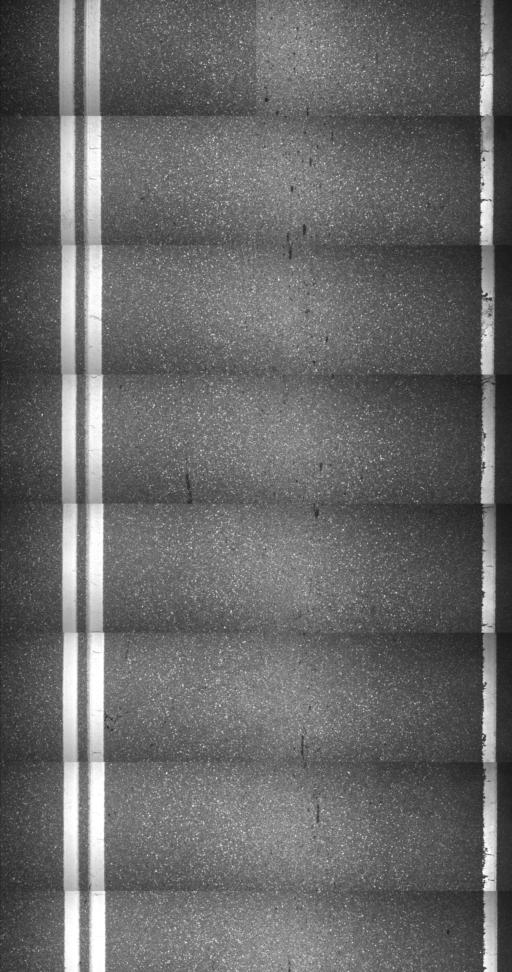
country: US
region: New Hampshire
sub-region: Grafton County
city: Haverhill
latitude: 44.0082
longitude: -72.1668
